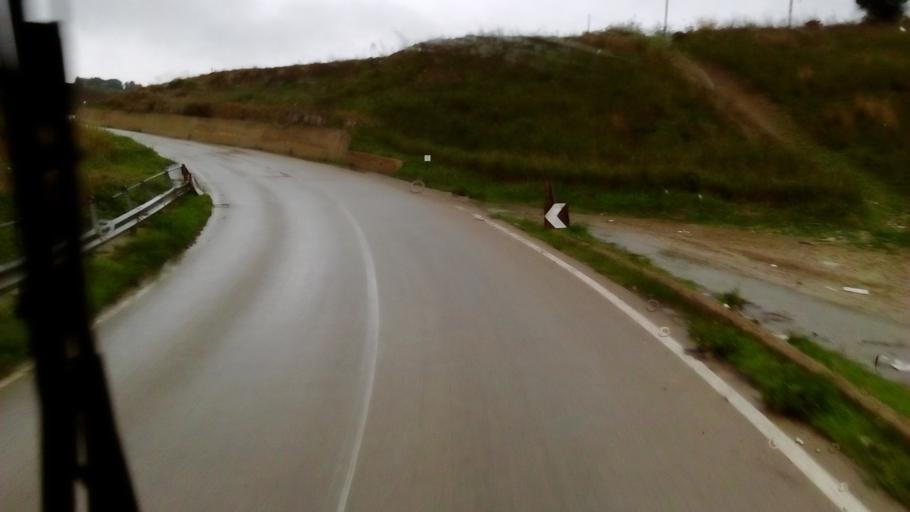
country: IT
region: Sicily
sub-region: Enna
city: Pietraperzia
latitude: 37.4373
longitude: 14.1736
